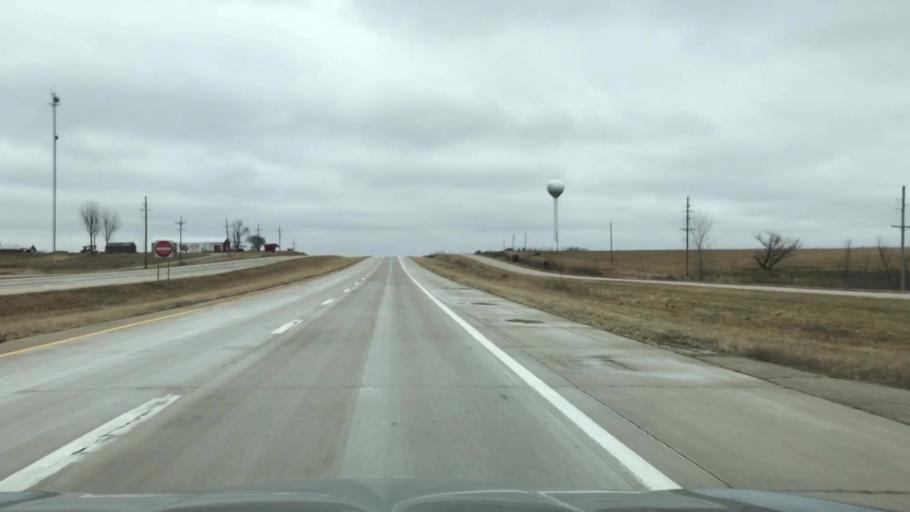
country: US
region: Missouri
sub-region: Livingston County
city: Chillicothe
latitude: 39.7393
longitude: -93.6633
